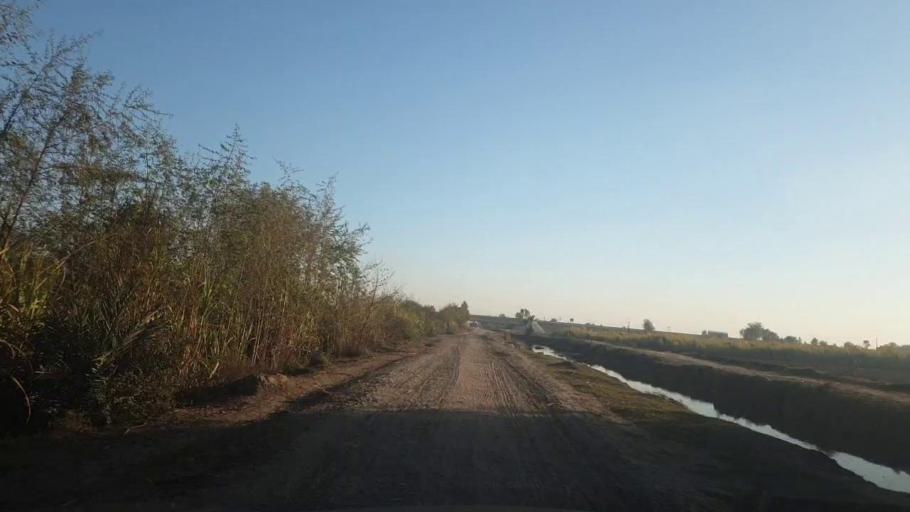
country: PK
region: Sindh
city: Ghotki
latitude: 28.0113
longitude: 69.2687
